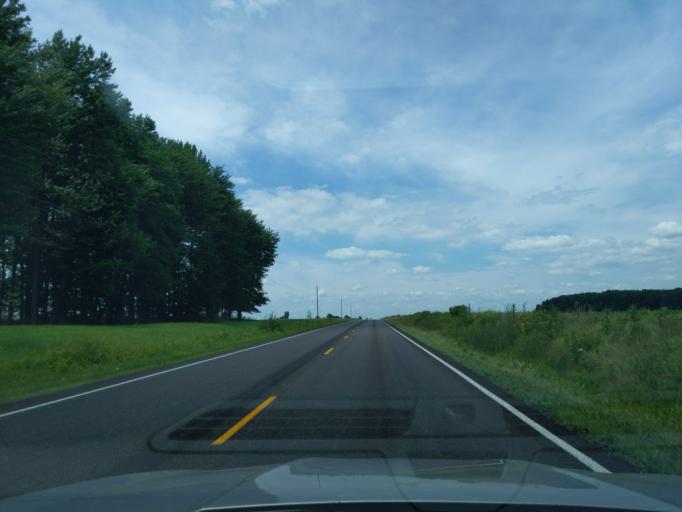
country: US
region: Indiana
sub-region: Ripley County
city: Osgood
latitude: 39.2515
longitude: -85.3591
